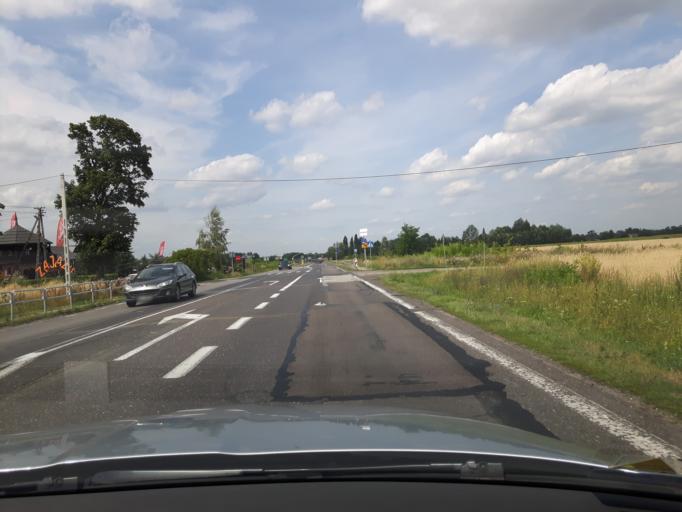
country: PL
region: Masovian Voivodeship
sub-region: Powiat plonski
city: Plonsk
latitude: 52.6858
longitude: 20.3595
